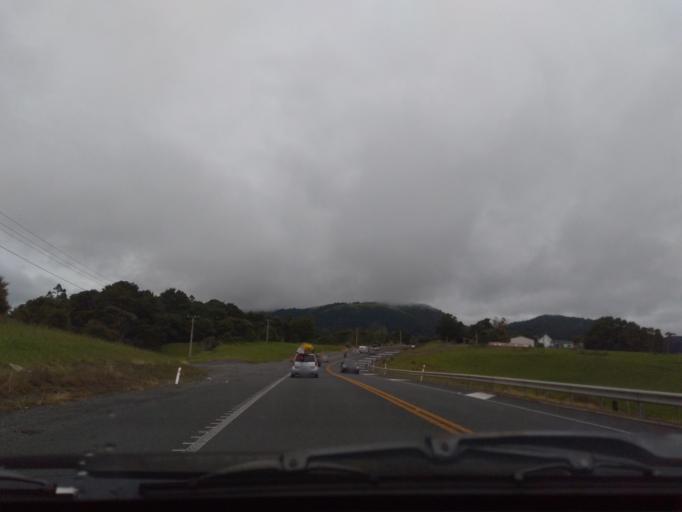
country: NZ
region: Auckland
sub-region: Auckland
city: Wellsford
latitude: -36.1428
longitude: 174.4345
